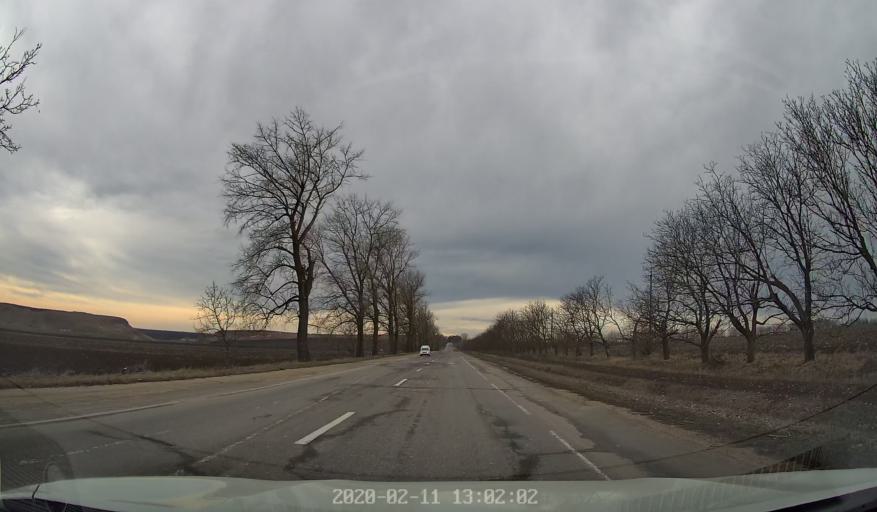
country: MD
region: Briceni
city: Briceni
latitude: 48.3163
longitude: 26.9900
